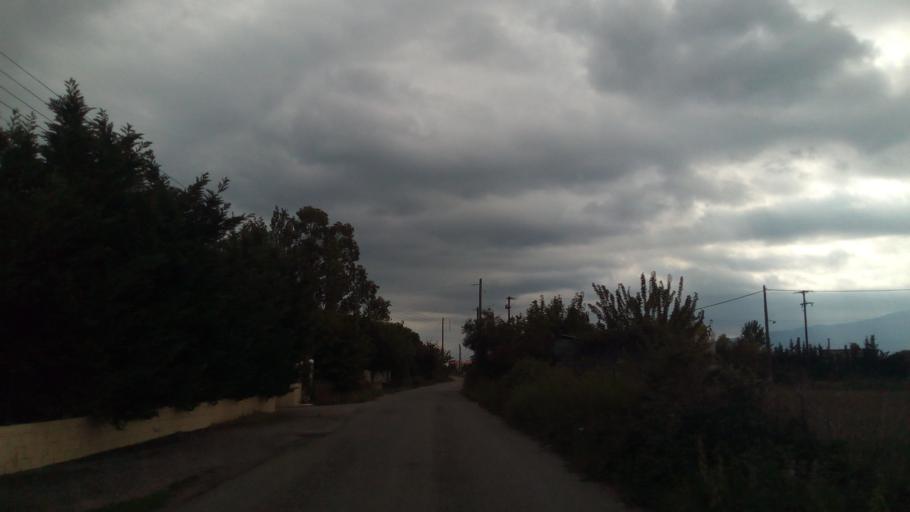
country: GR
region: West Greece
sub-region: Nomos Aitolias kai Akarnanias
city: Nafpaktos
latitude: 38.3966
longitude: 21.9139
